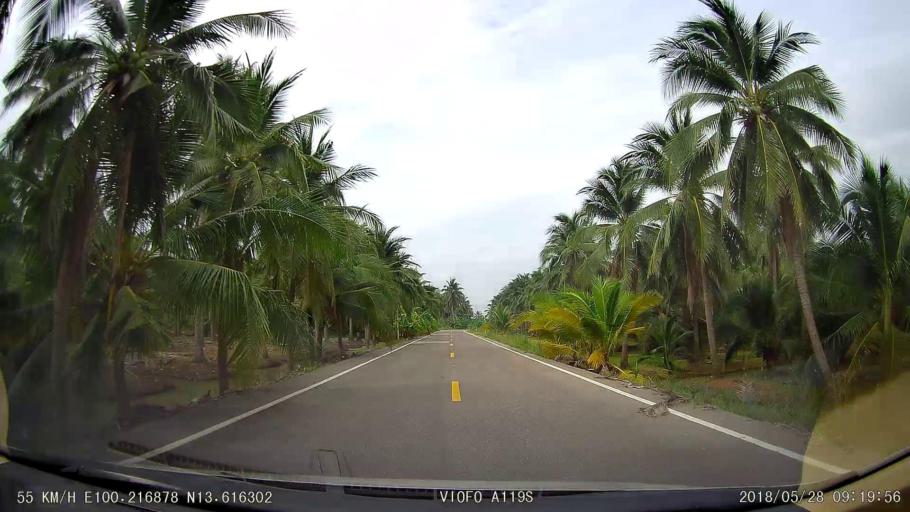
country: TH
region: Samut Sakhon
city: Krathum Baen
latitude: 13.6158
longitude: 100.2141
